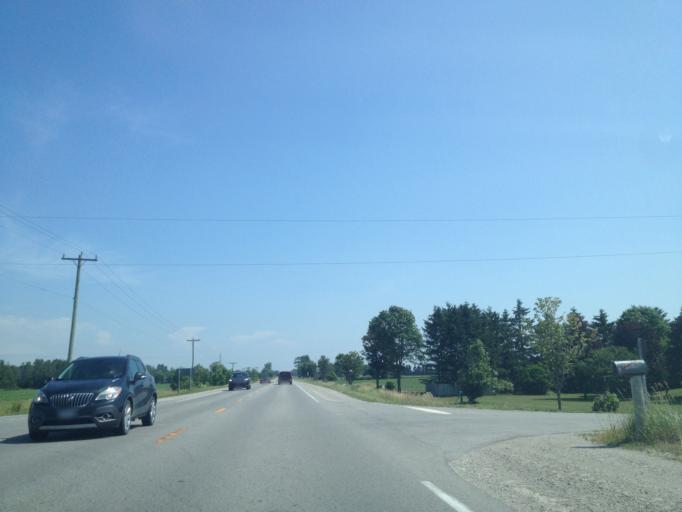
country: CA
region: Ontario
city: Huron East
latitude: 43.4363
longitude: -81.2249
